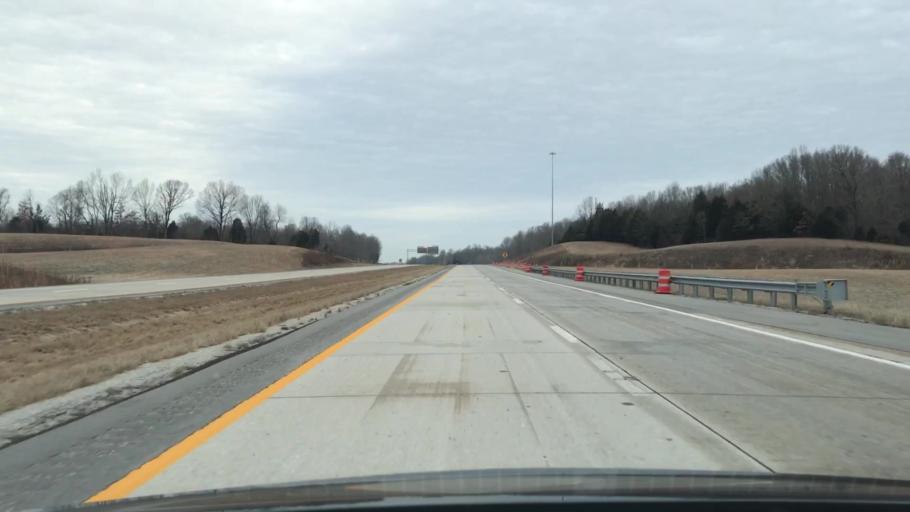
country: US
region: Kentucky
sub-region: Ohio County
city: Beaver Dam
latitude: 37.3859
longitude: -86.8098
